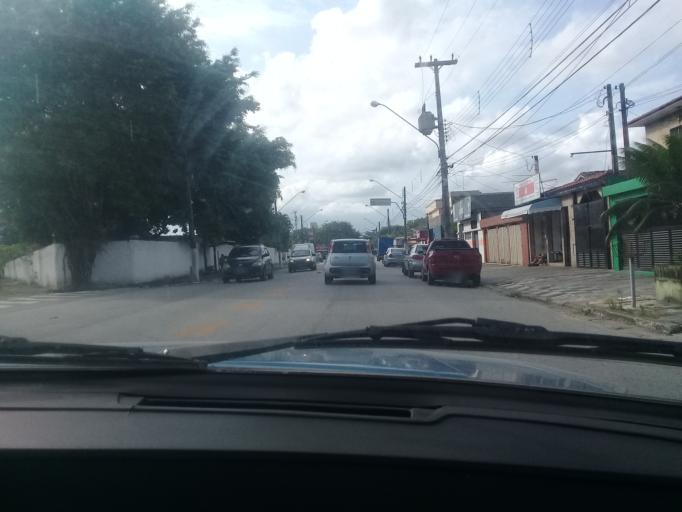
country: BR
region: Sao Paulo
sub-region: Guaruja
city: Guaruja
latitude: -23.9958
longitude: -46.2751
